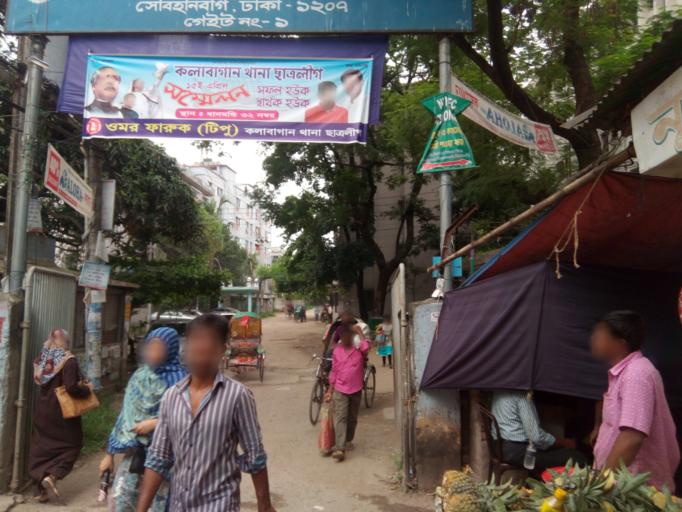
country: BD
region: Dhaka
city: Azimpur
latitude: 23.7555
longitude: 90.3771
